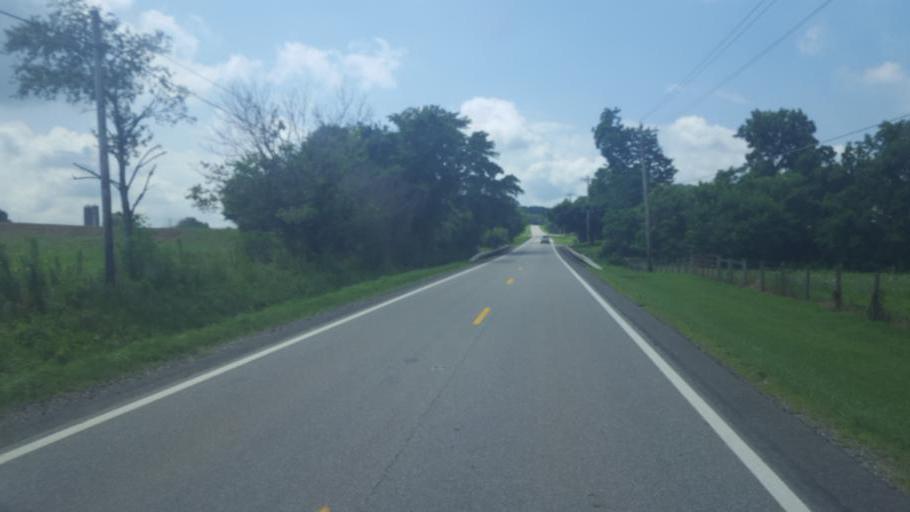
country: US
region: Ohio
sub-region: Pickaway County
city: Circleville
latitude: 39.5887
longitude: -82.7590
